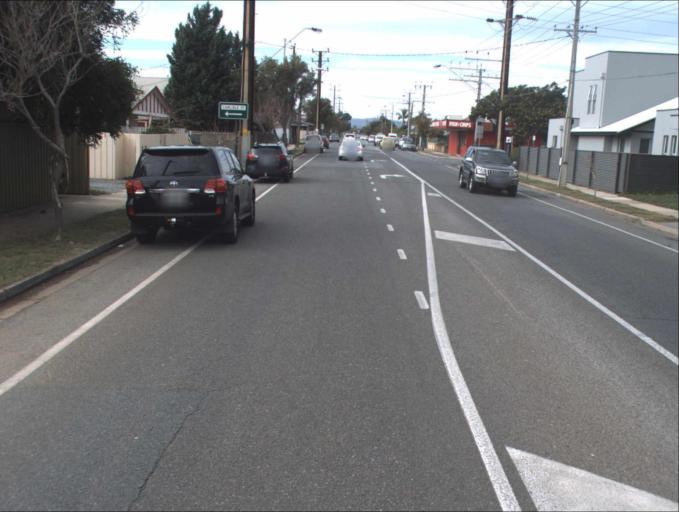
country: AU
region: South Australia
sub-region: Charles Sturt
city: West Lakes Shore
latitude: -34.8512
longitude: 138.4877
